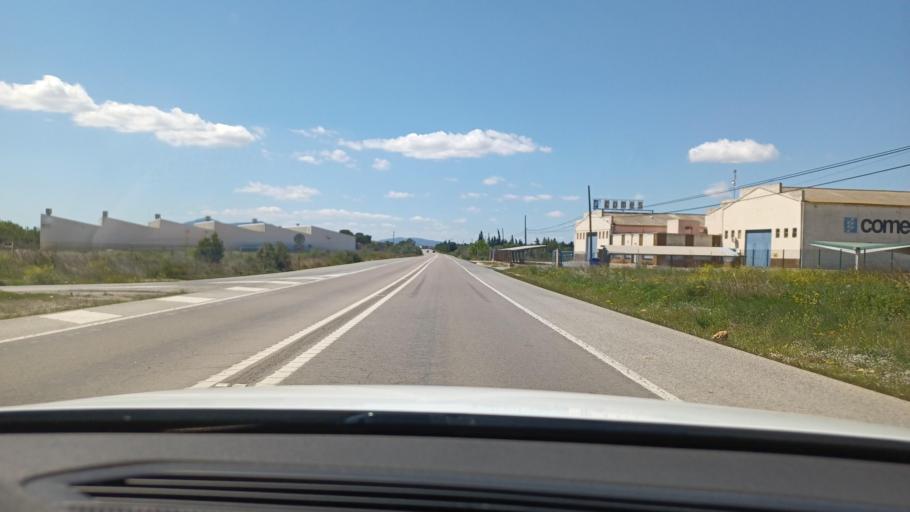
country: ES
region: Catalonia
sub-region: Provincia de Tarragona
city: Camarles
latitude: 40.7746
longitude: 0.6587
